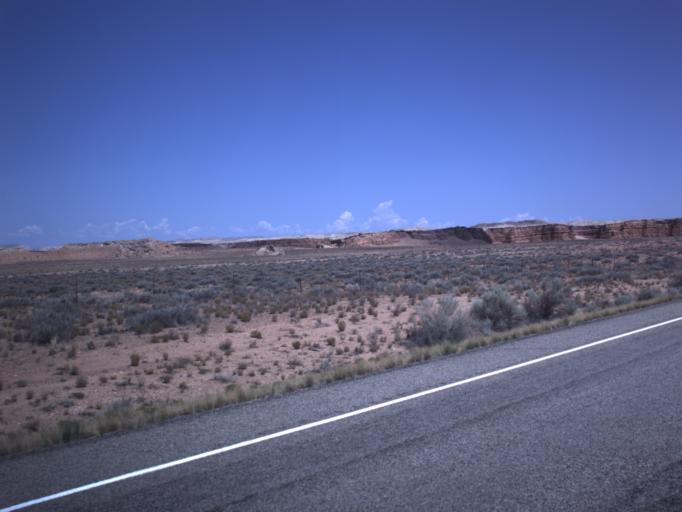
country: US
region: Utah
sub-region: Emery County
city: Ferron
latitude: 38.4221
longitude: -110.6929
